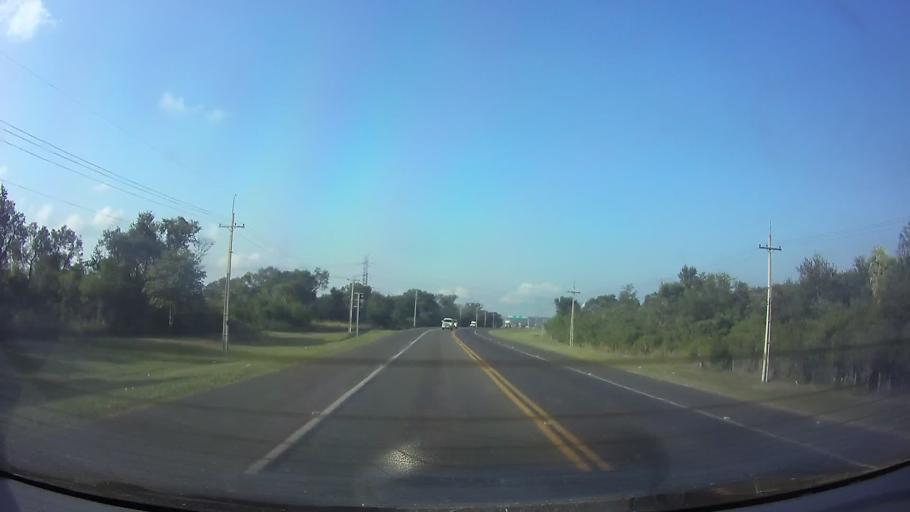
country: PY
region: Central
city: Limpio
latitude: -25.1156
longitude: -57.4262
